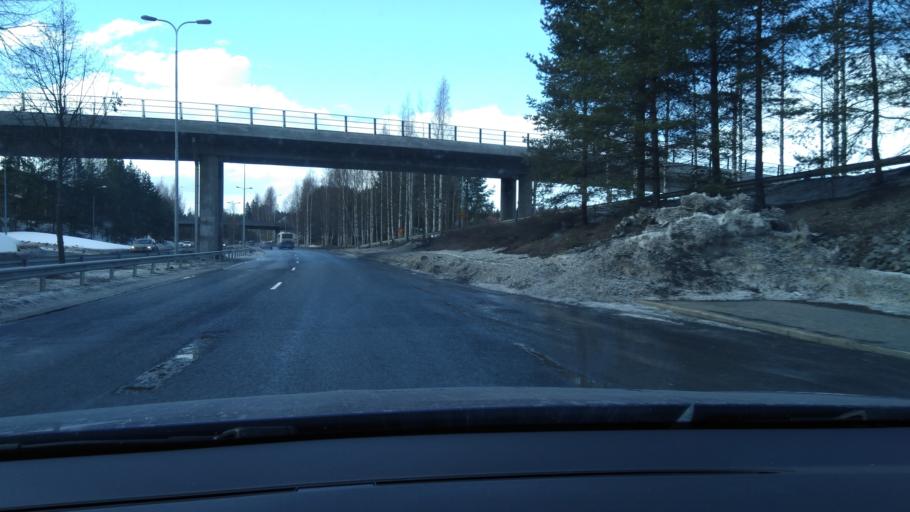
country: FI
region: Pirkanmaa
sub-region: Tampere
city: Tampere
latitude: 61.5027
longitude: 23.8051
